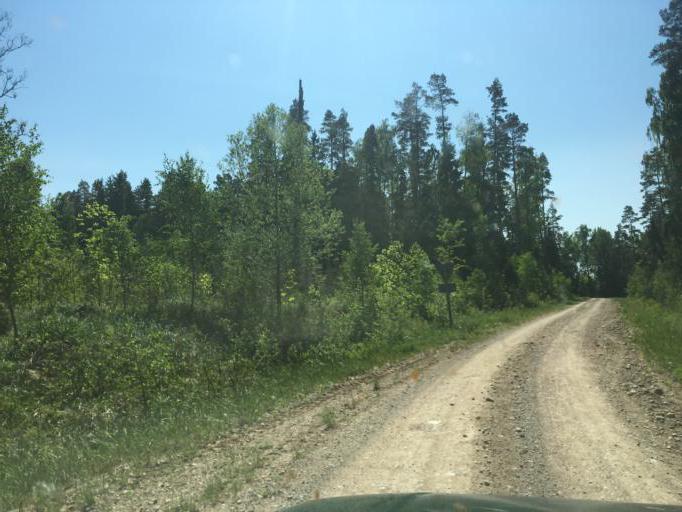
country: LV
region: Talsu Rajons
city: Valdemarpils
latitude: 57.4489
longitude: 22.6561
